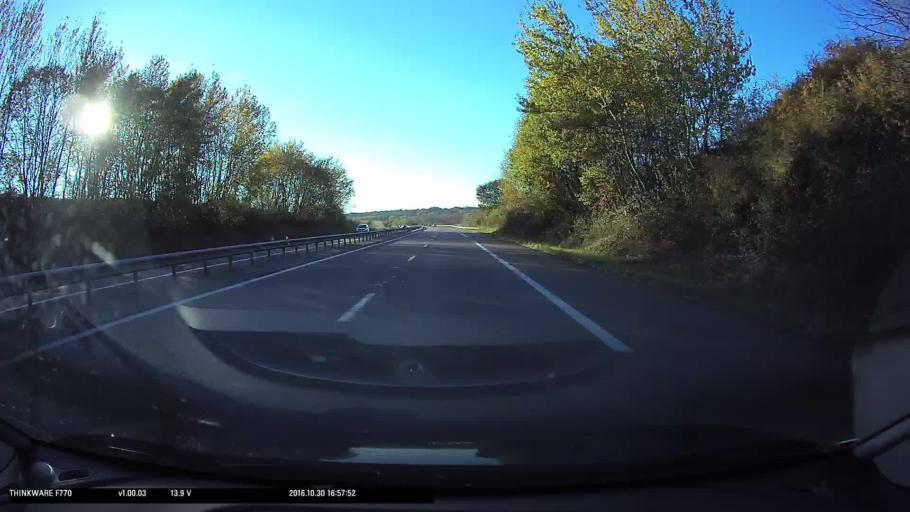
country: FR
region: Franche-Comte
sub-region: Departement du Doubs
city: Saint-Vit
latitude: 47.1937
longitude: 5.7740
